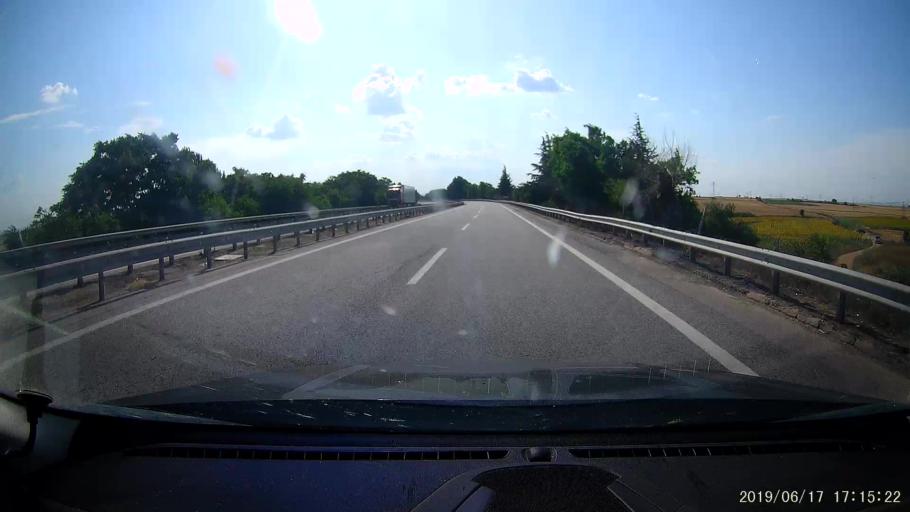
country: GR
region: East Macedonia and Thrace
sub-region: Nomos Evrou
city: Kastanies
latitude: 41.7018
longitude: 26.4976
